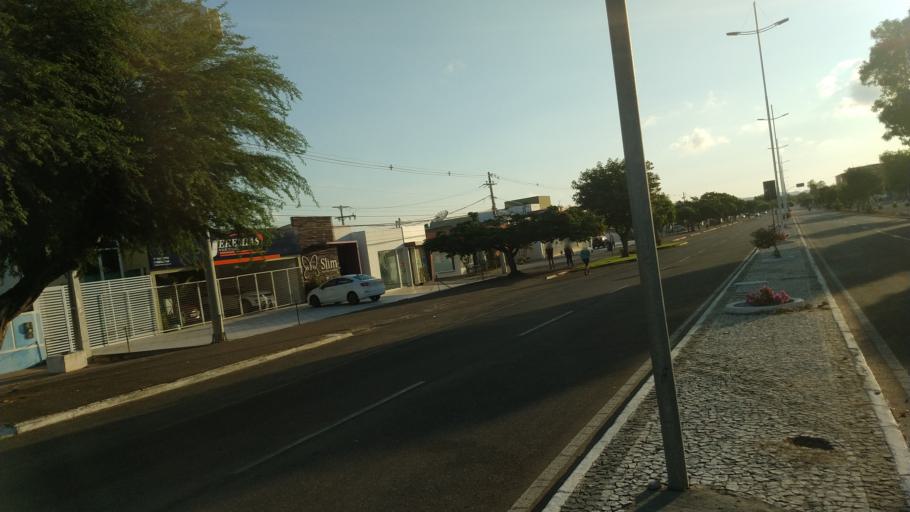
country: BR
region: Bahia
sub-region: Paulo Afonso
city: Paulo Afonso
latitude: -9.3984
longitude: -38.2271
